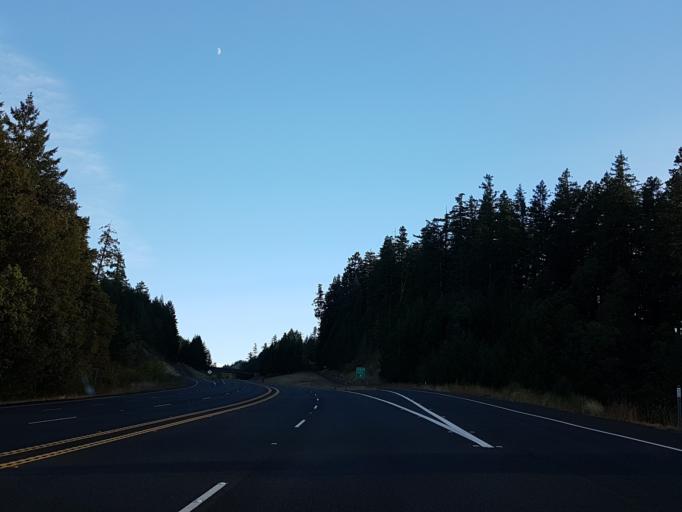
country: US
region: California
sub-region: Humboldt County
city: Redway
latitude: 39.9489
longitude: -123.7812
